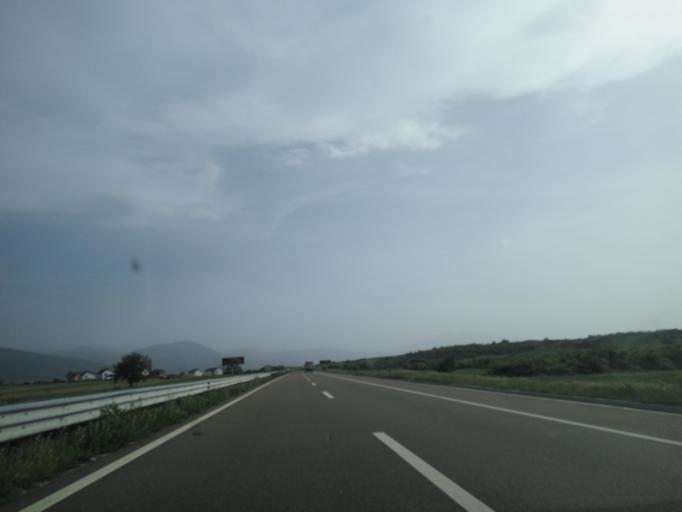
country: XK
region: Prizren
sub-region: Komuna e Therandes
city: Leshan
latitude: 42.2970
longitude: 20.7618
